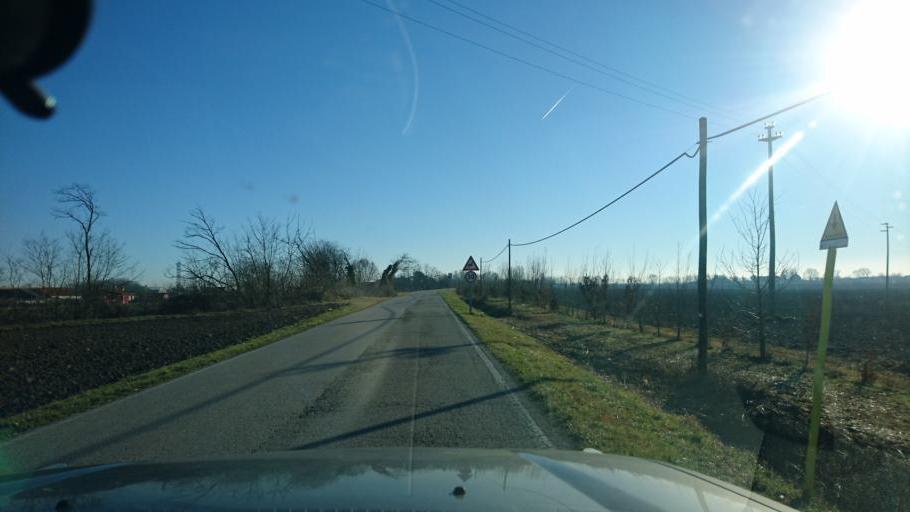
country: IT
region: Veneto
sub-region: Provincia di Venezia
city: Boscochiaro
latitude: 45.1169
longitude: 12.1334
